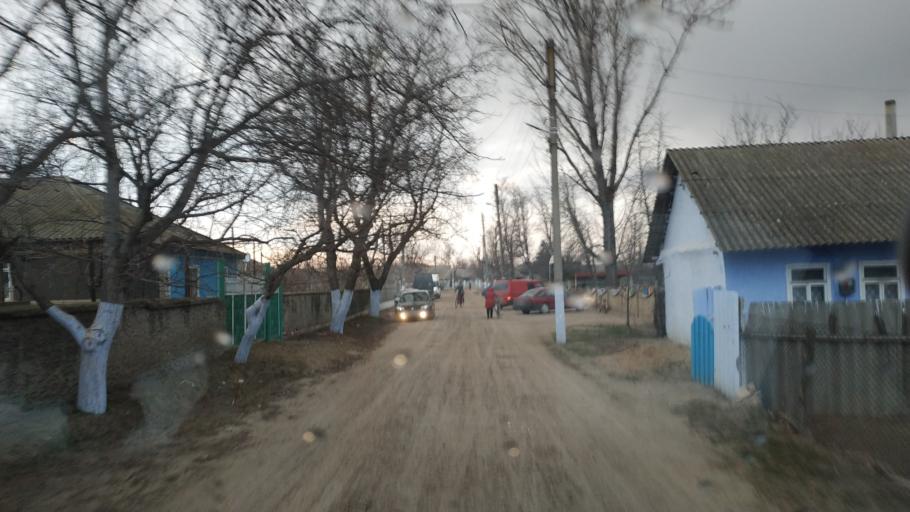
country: MD
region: Telenesti
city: Grigoriopol
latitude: 47.0931
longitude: 29.3465
